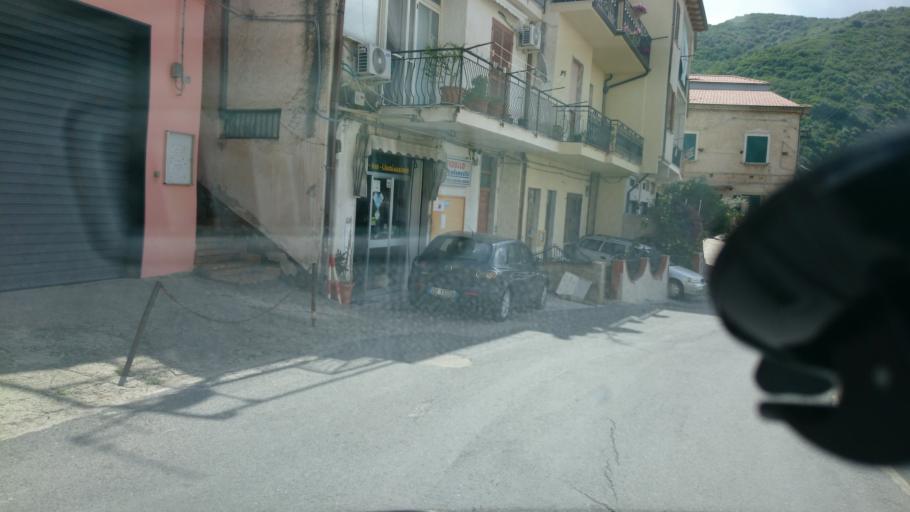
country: IT
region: Campania
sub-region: Provincia di Salerno
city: Pisciotta
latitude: 40.1093
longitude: 15.2349
